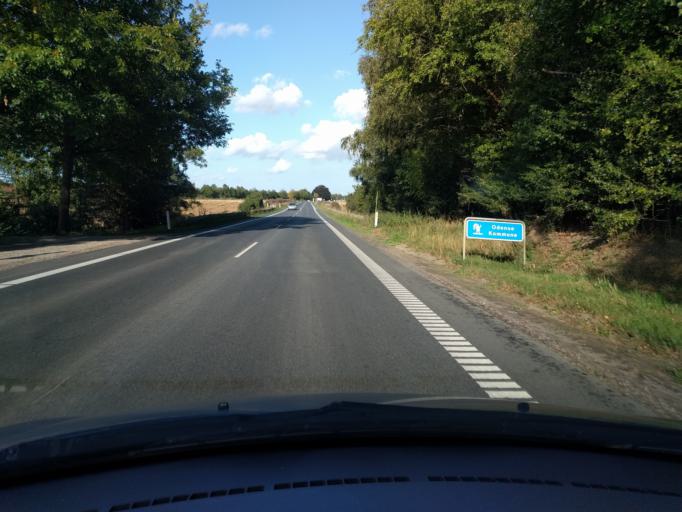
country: DK
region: South Denmark
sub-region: Odense Kommune
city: Bellinge
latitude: 55.3132
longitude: 10.2703
